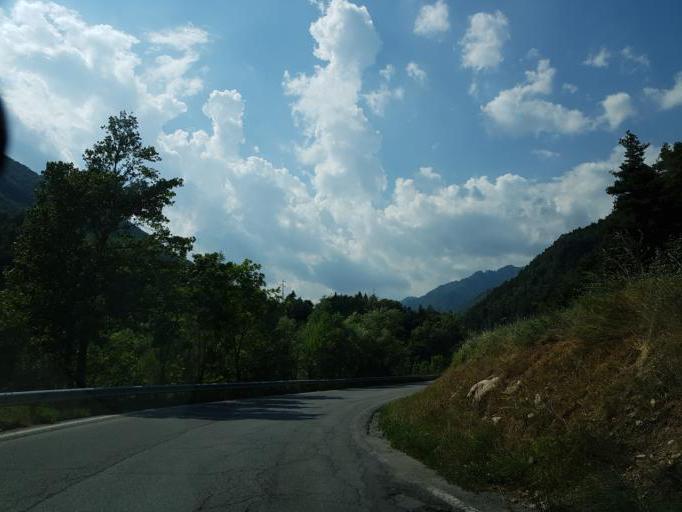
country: IT
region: Piedmont
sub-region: Provincia di Cuneo
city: Macra
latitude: 44.4935
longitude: 7.2054
